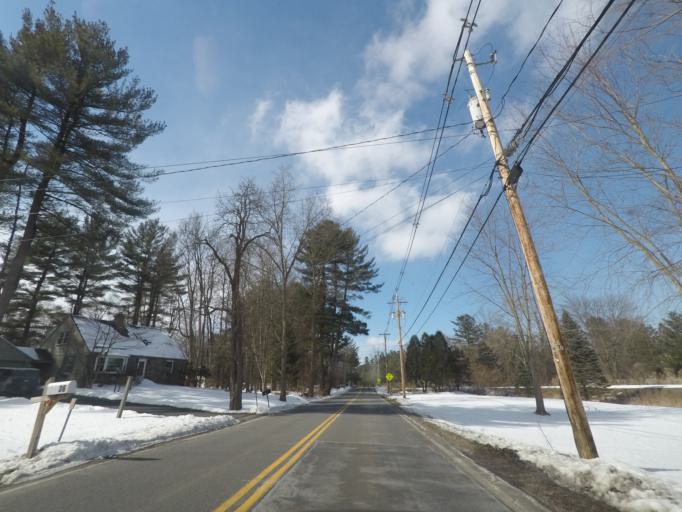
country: US
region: New York
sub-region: Albany County
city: Delmar
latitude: 42.6304
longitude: -73.8701
